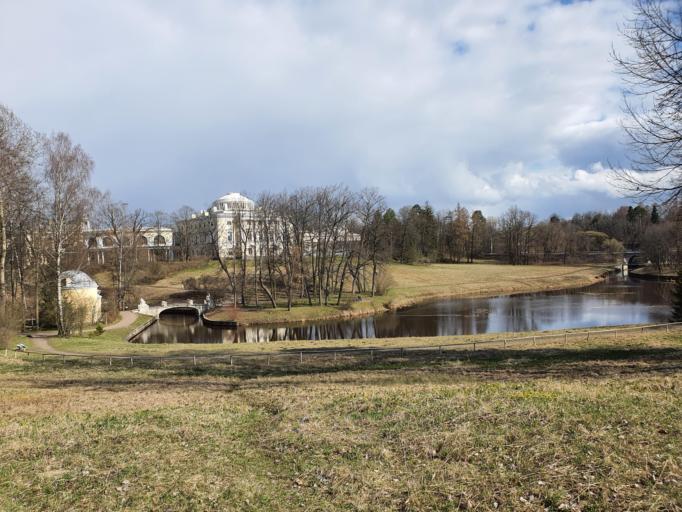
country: RU
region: St.-Petersburg
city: Pavlovsk
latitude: 59.6864
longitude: 30.4487
